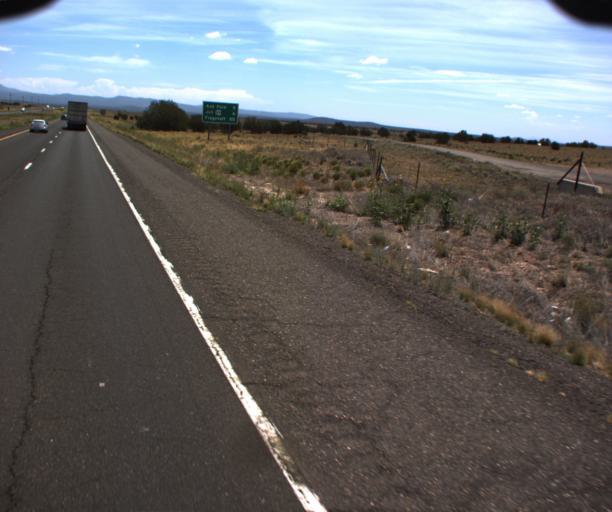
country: US
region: Arizona
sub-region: Yavapai County
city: Paulden
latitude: 35.2263
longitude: -112.5701
